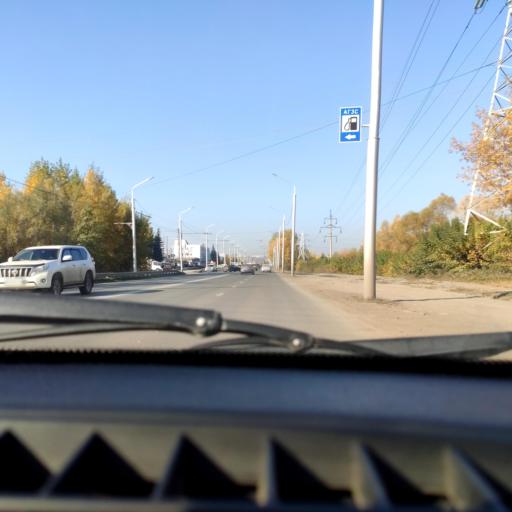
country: RU
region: Bashkortostan
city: Ufa
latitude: 54.7909
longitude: 56.0932
